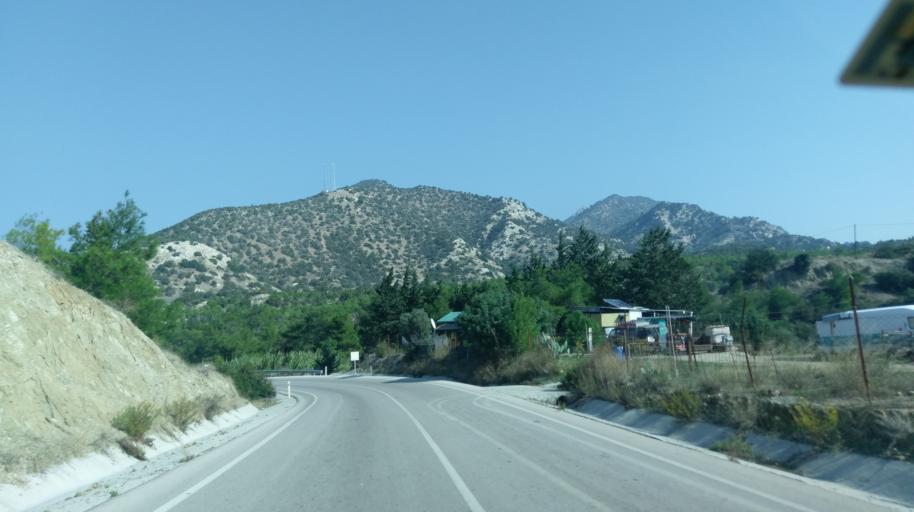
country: CY
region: Ammochostos
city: Lefkonoiko
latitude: 35.3421
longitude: 33.7122
